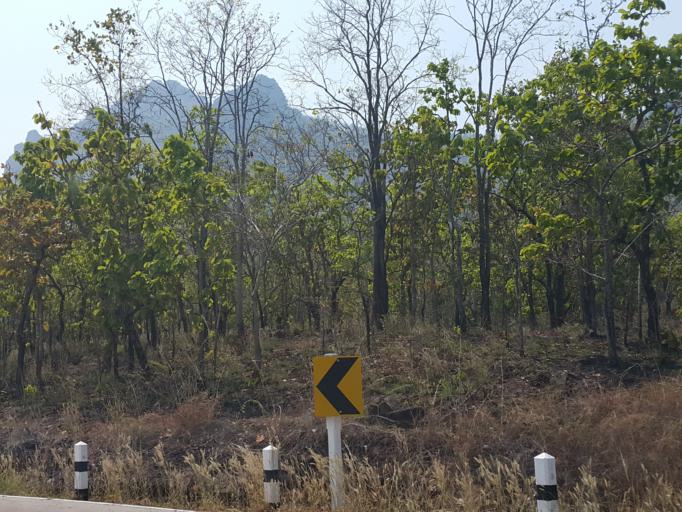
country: TH
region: Lampang
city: Chae Hom
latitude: 18.7461
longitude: 99.5456
